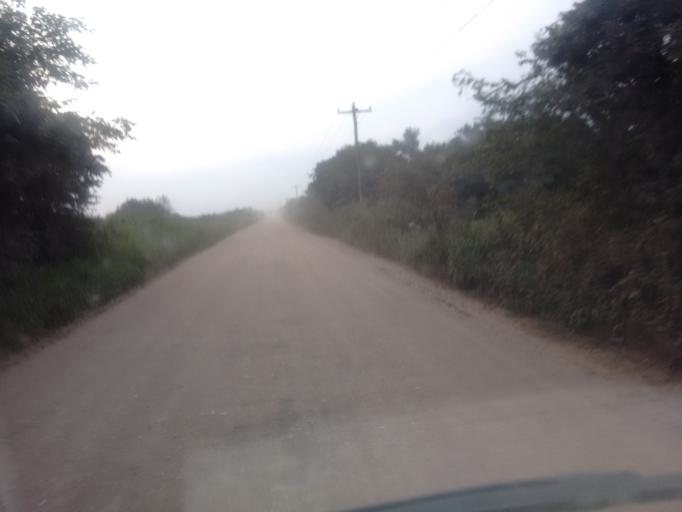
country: BR
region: Rio Grande do Sul
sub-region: Camaqua
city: Camaqua
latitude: -30.9188
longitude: -51.8022
